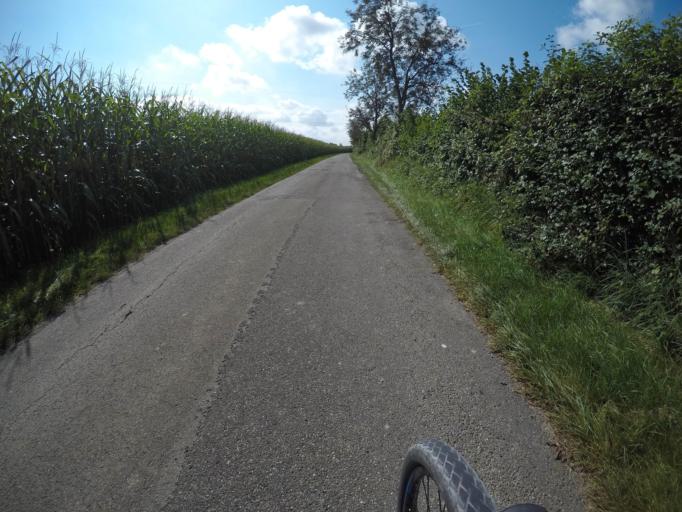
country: DE
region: Bavaria
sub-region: Swabia
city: Tapfheim
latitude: 48.6385
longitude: 10.6955
